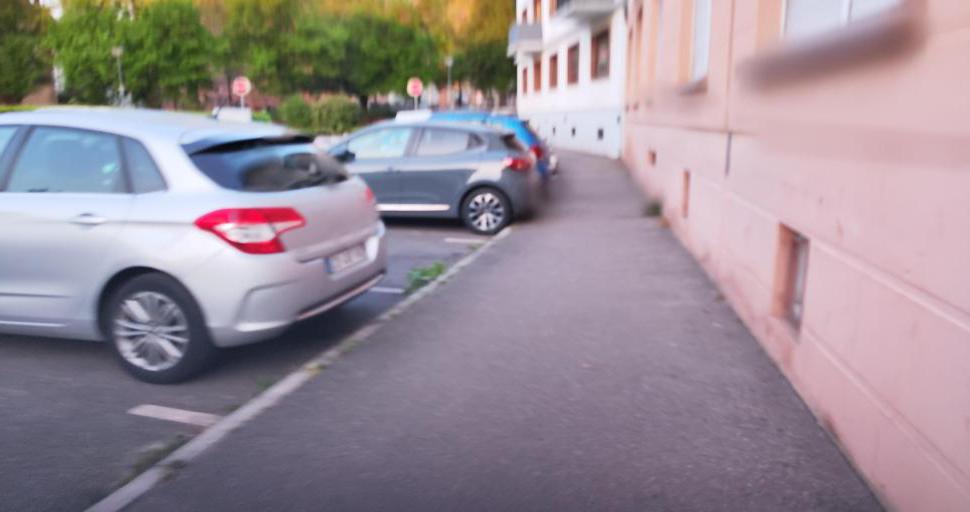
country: FR
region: Alsace
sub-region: Departement du Bas-Rhin
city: Selestat
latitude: 48.2608
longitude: 7.4583
